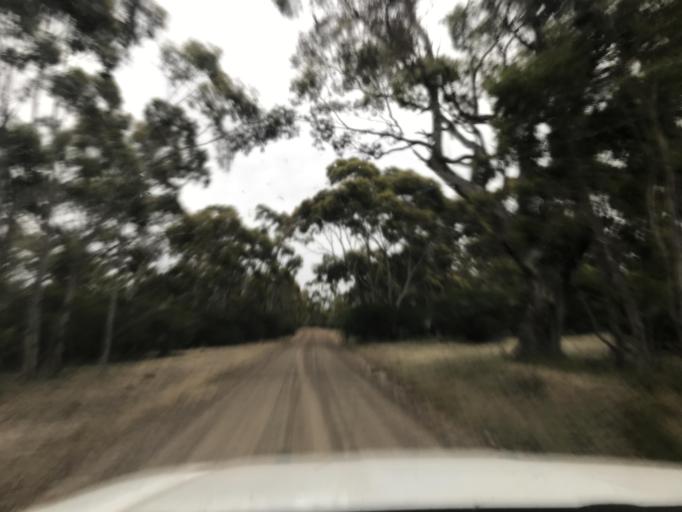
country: AU
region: South Australia
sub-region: Wattle Range
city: Penola
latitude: -37.0945
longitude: 141.5171
